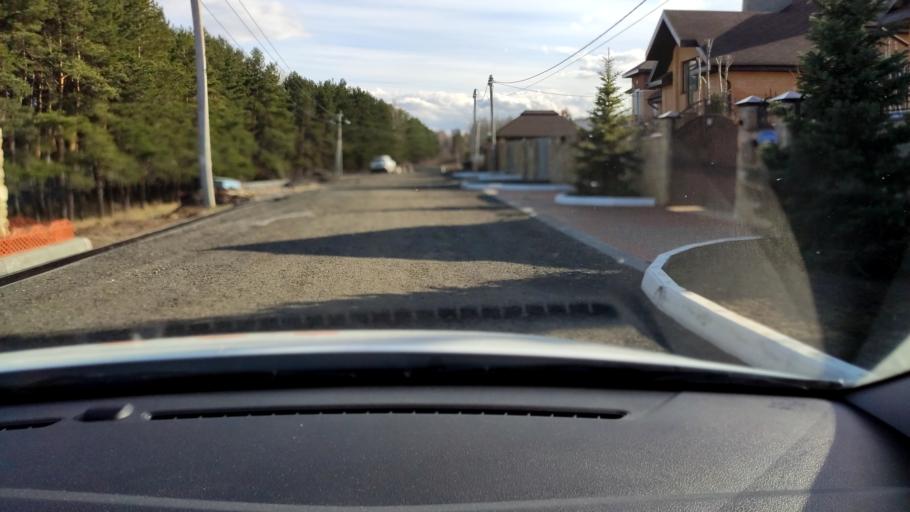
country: RU
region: Tatarstan
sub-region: Gorod Kazan'
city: Kazan
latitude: 55.7805
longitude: 49.2478
